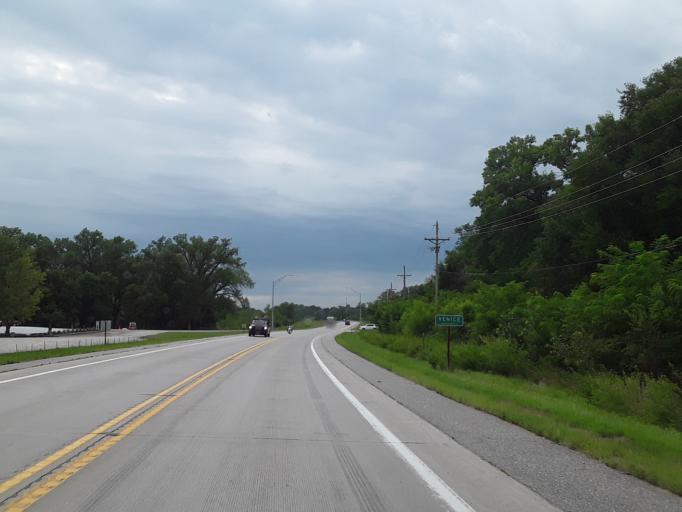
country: US
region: Nebraska
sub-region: Saunders County
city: Yutan
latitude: 41.2338
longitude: -96.3512
